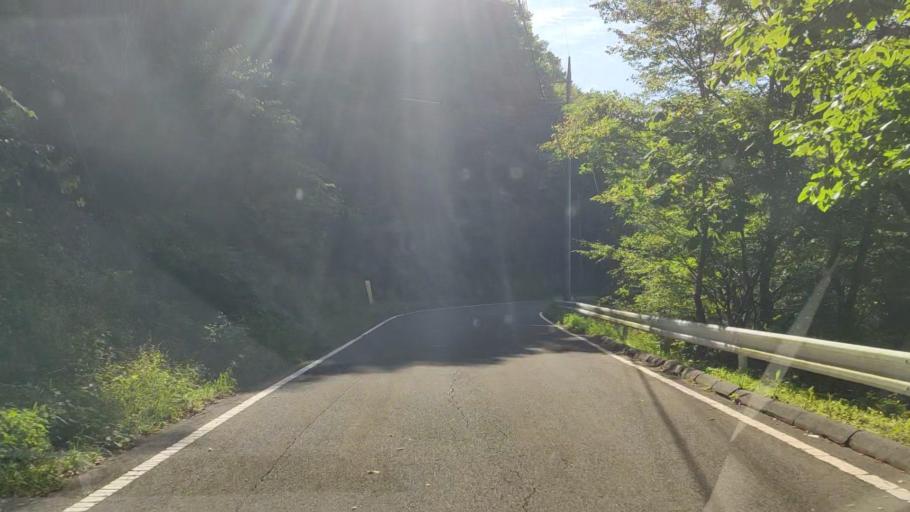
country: JP
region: Gunma
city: Nakanojomachi
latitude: 36.5975
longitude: 138.6910
